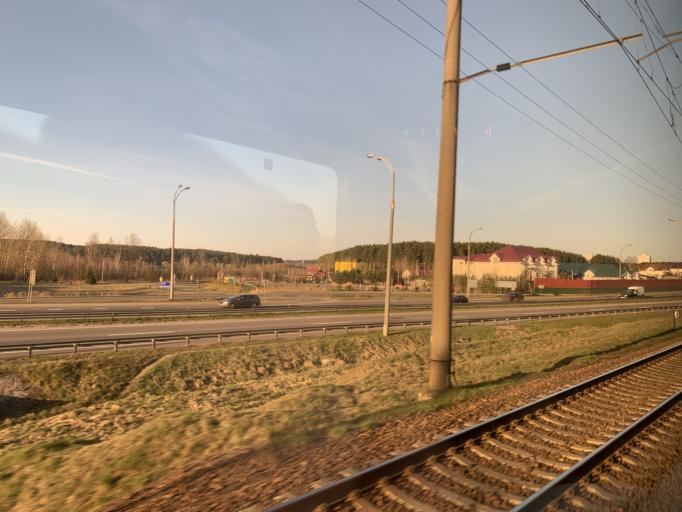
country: BY
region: Minsk
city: Zhdanovichy
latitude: 53.9521
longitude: 27.4072
